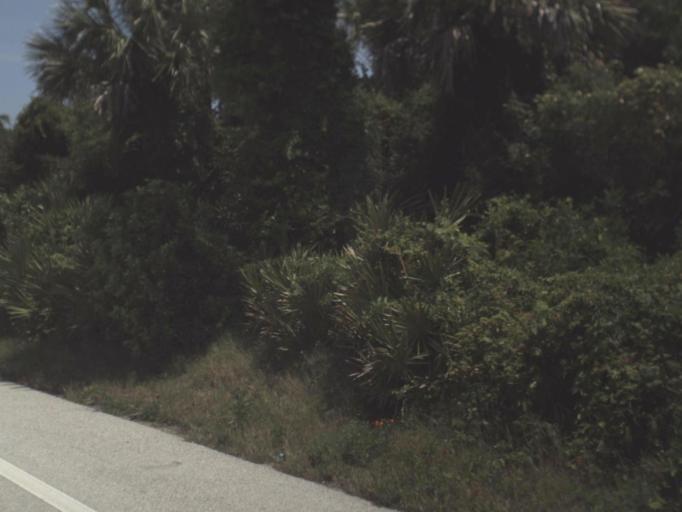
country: US
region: Florida
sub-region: Saint Johns County
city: Palm Valley
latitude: 30.1005
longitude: -81.3416
